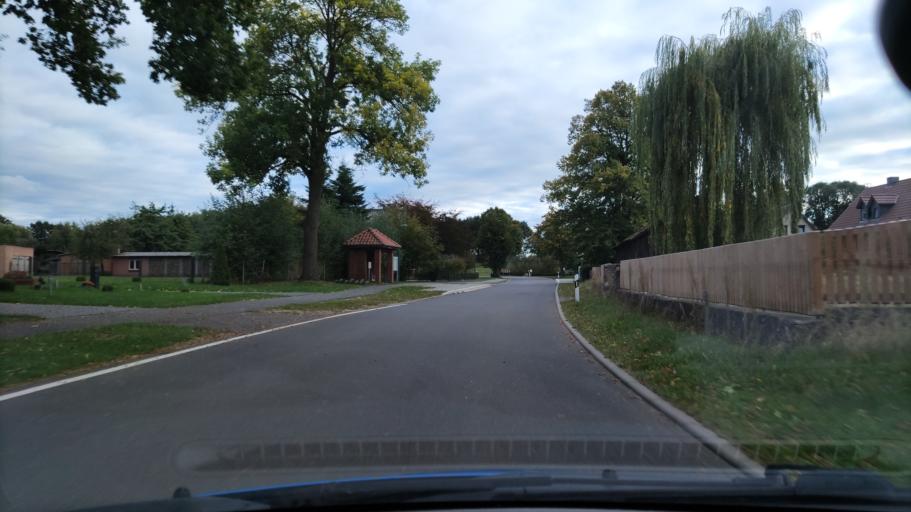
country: DE
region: Mecklenburg-Vorpommern
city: Boizenburg
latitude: 53.4170
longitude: 10.8470
